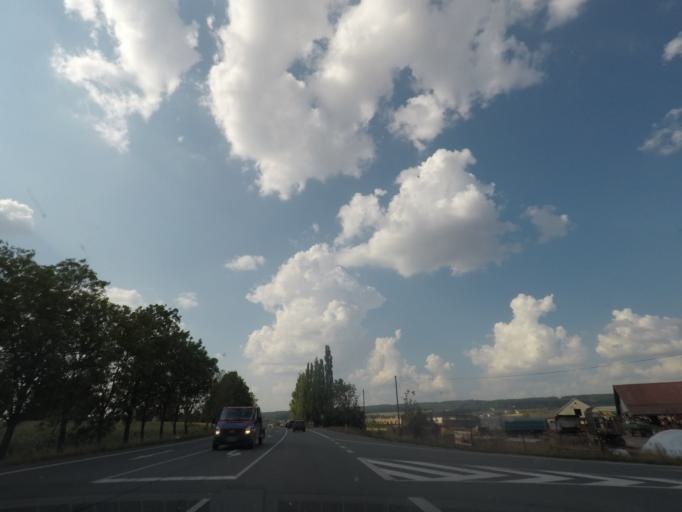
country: CZ
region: Kralovehradecky
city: Dvur Kralove nad Labem
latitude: 50.4178
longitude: 15.8835
